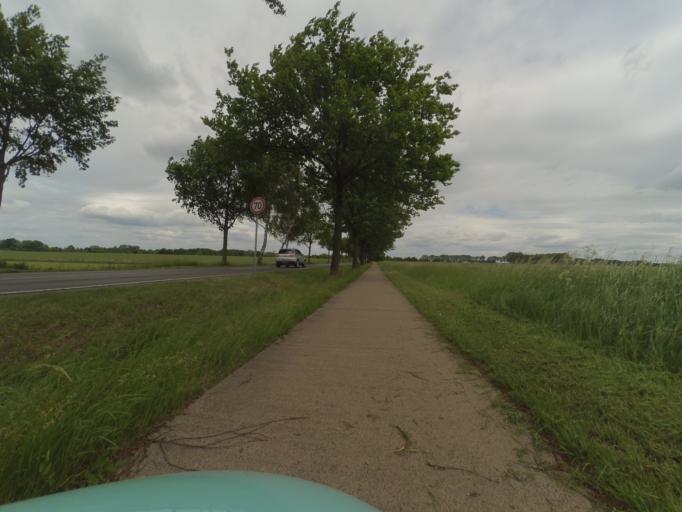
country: DE
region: Lower Saxony
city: Hagenburg
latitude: 52.4414
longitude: 9.3515
